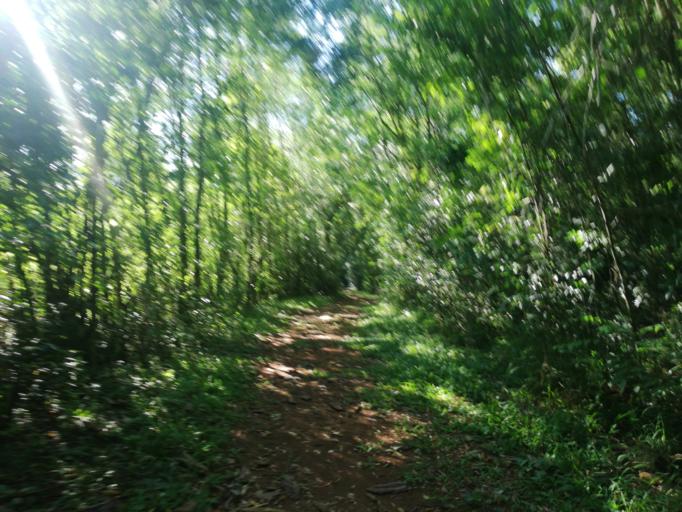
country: AR
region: Misiones
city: Cerro Azul
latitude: -27.7440
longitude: -55.5641
